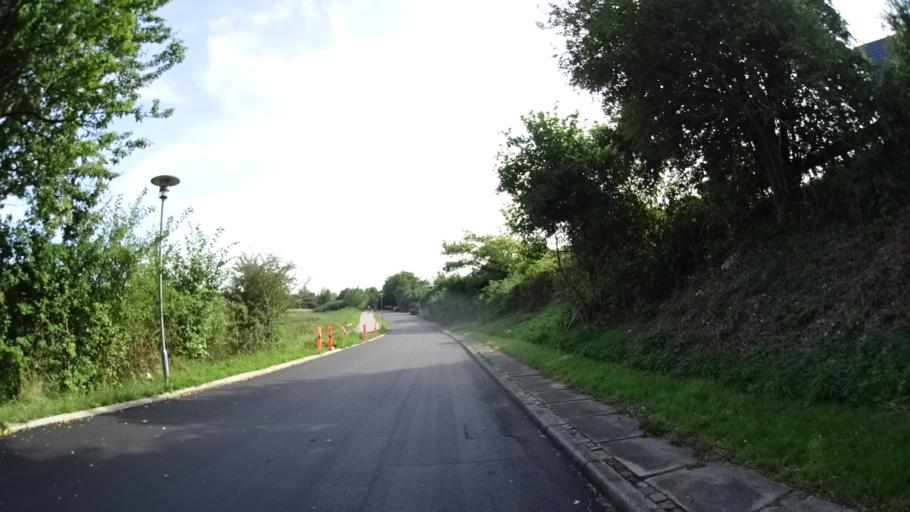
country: DK
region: Central Jutland
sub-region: Arhus Kommune
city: Stavtrup
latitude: 56.1424
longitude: 10.1548
